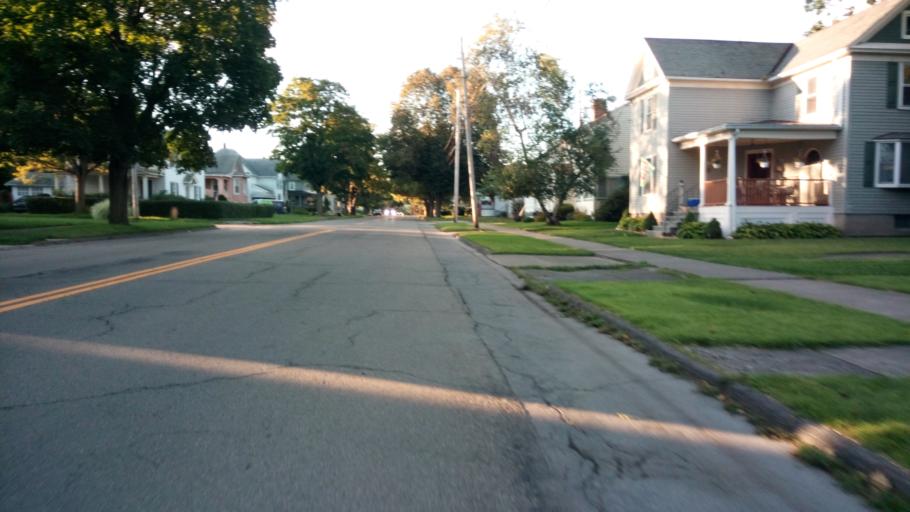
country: US
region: New York
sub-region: Chemung County
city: Elmira
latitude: 42.0987
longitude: -76.8198
